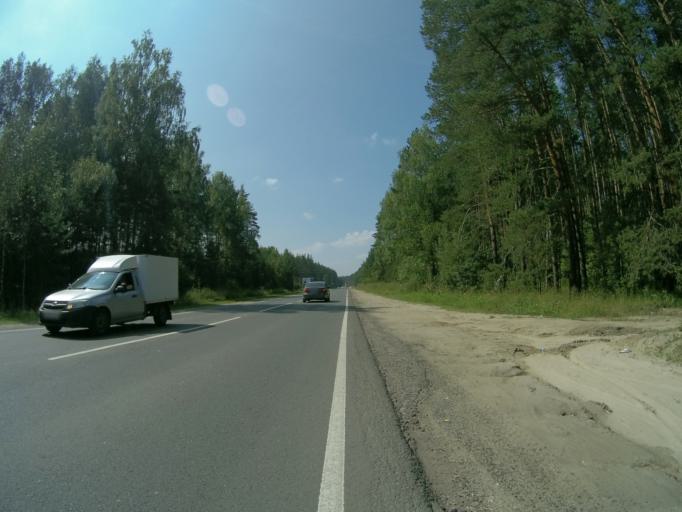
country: RU
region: Vladimir
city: Gus'-Khrustal'nyy
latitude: 55.6425
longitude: 40.7083
